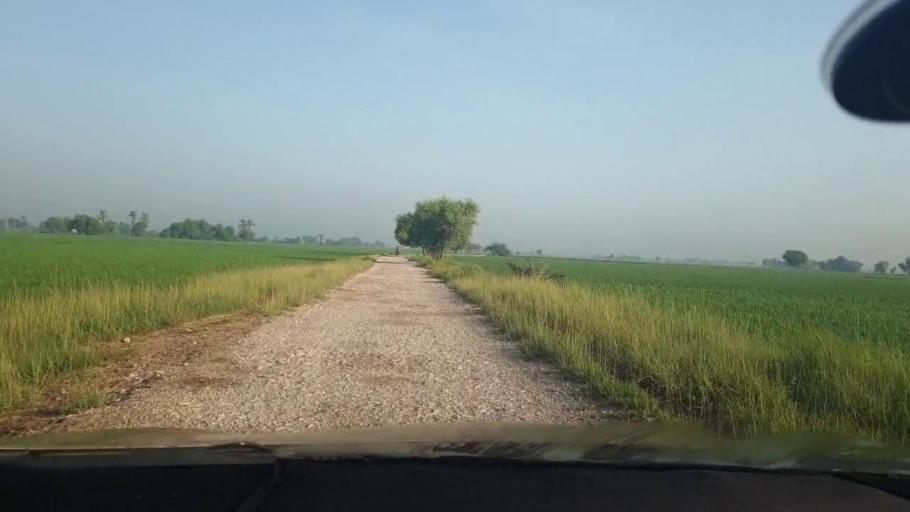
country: PK
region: Sindh
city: Kambar
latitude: 27.6183
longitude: 68.0193
